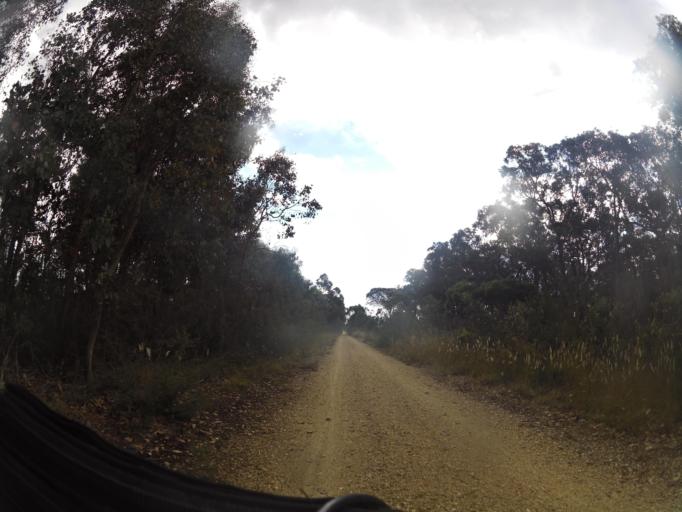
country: AU
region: Victoria
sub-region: Wellington
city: Heyfield
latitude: -38.0351
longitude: 146.6554
